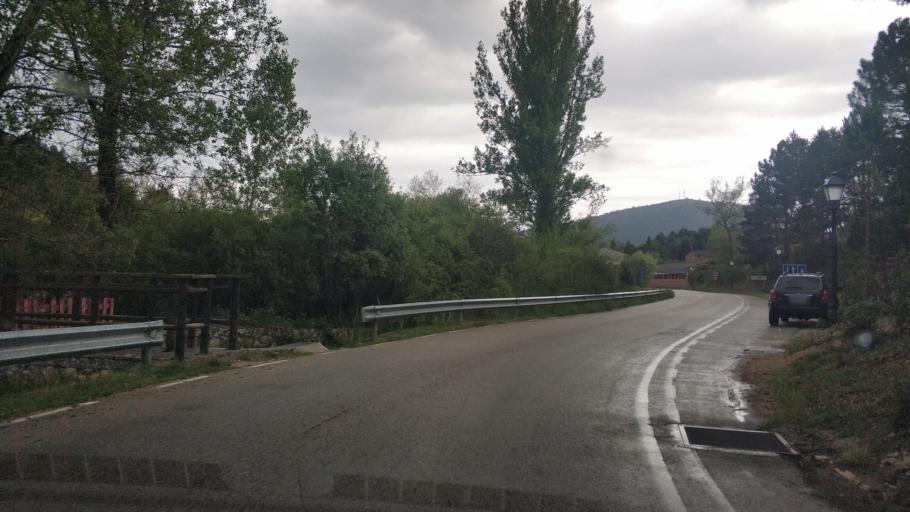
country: ES
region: Castille and Leon
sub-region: Provincia de Soria
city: San Leonardo de Yague
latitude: 41.8349
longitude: -3.0662
